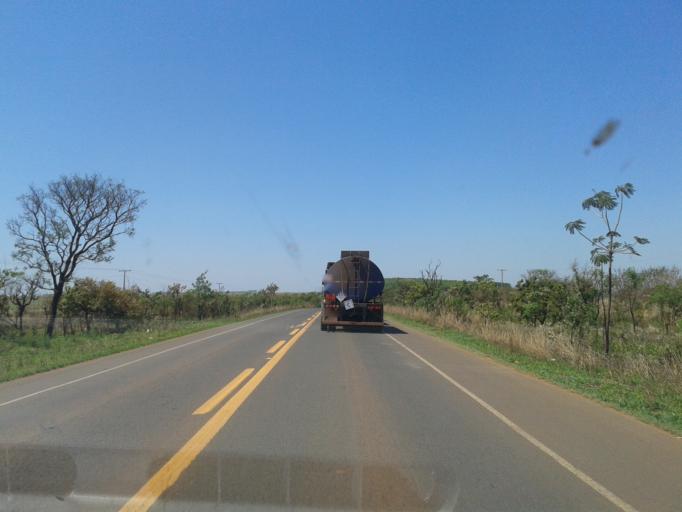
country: BR
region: Minas Gerais
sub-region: Araxa
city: Araxa
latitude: -19.3230
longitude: -47.3834
